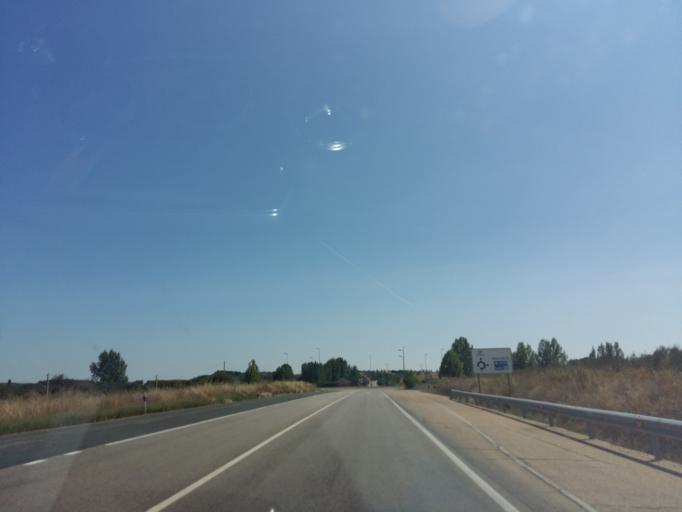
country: ES
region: Castille and Leon
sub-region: Provincia de Leon
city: San Justo de la Vega
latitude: 42.4369
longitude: -6.0338
